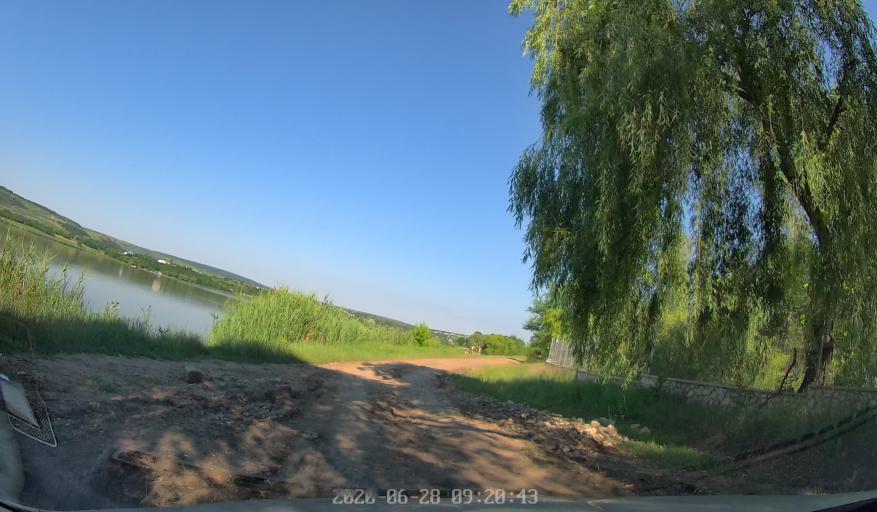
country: MD
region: Laloveni
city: Ialoveni
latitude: 46.9827
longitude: 28.7039
